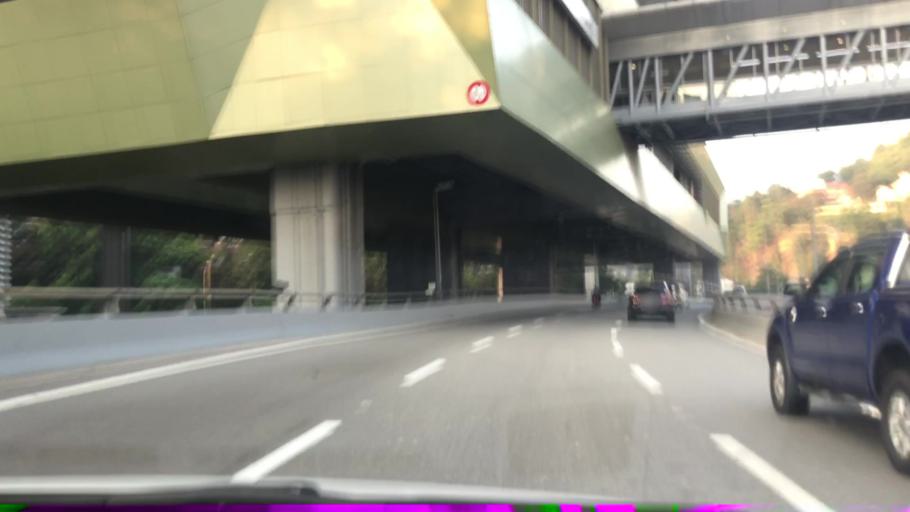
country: MY
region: Kuala Lumpur
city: Kuala Lumpur
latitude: 3.1437
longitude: 101.6630
